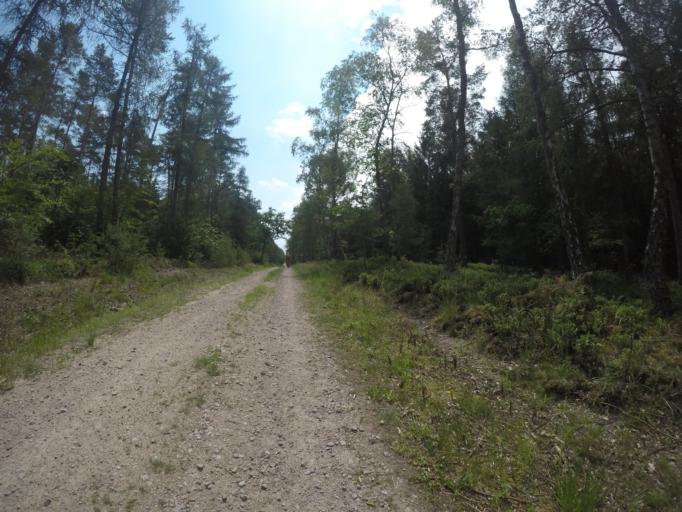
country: DE
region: Lower Saxony
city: Jesteburg
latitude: 53.2647
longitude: 9.9307
